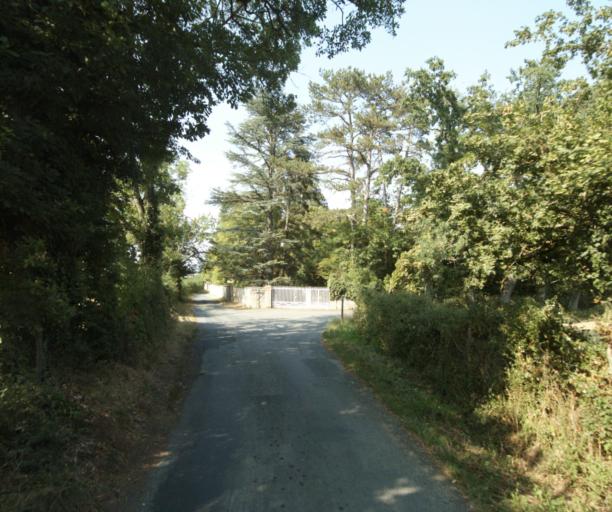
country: FR
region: Rhone-Alpes
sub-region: Departement du Rhone
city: Bully
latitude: 45.8341
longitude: 4.5871
